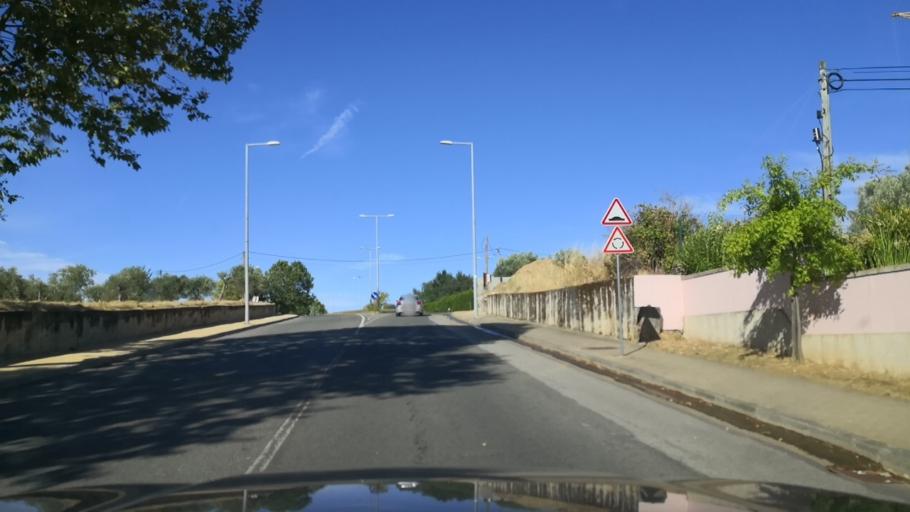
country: PT
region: Vila Real
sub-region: Murca
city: Murca
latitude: 41.4019
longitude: -7.4532
